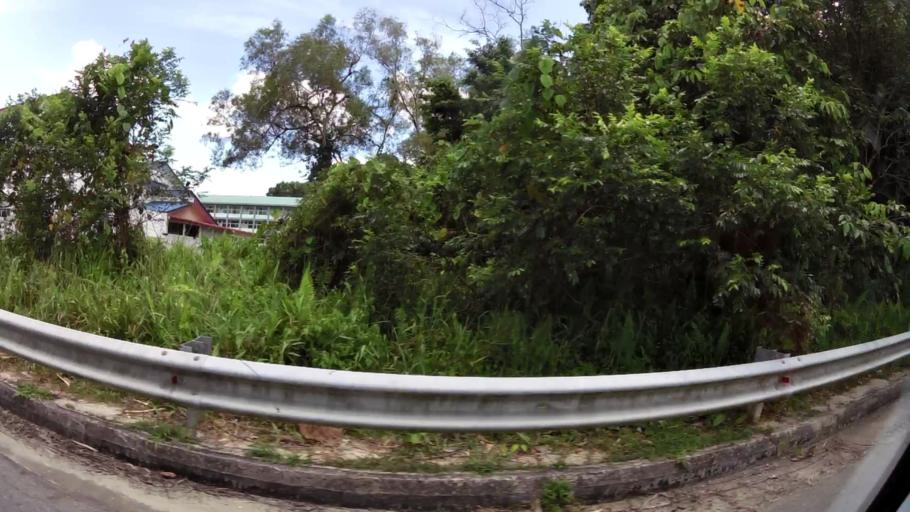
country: BN
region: Brunei and Muara
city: Bandar Seri Begawan
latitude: 4.9293
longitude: 114.9606
